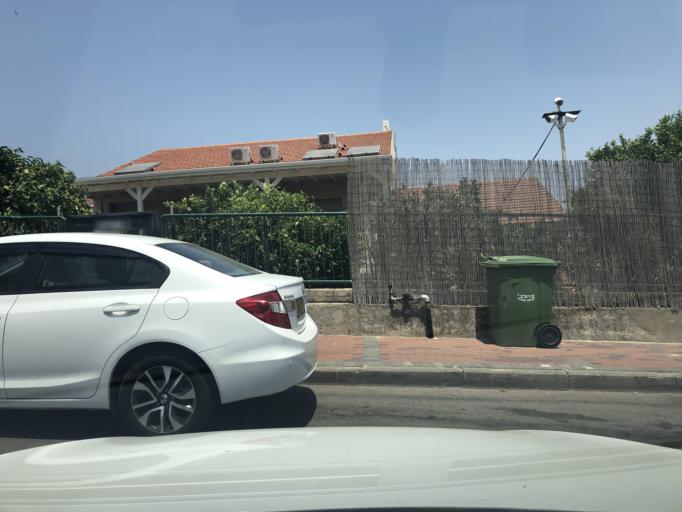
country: IL
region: Haifa
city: Daliyat el Karmil
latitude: 32.6589
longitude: 35.1114
